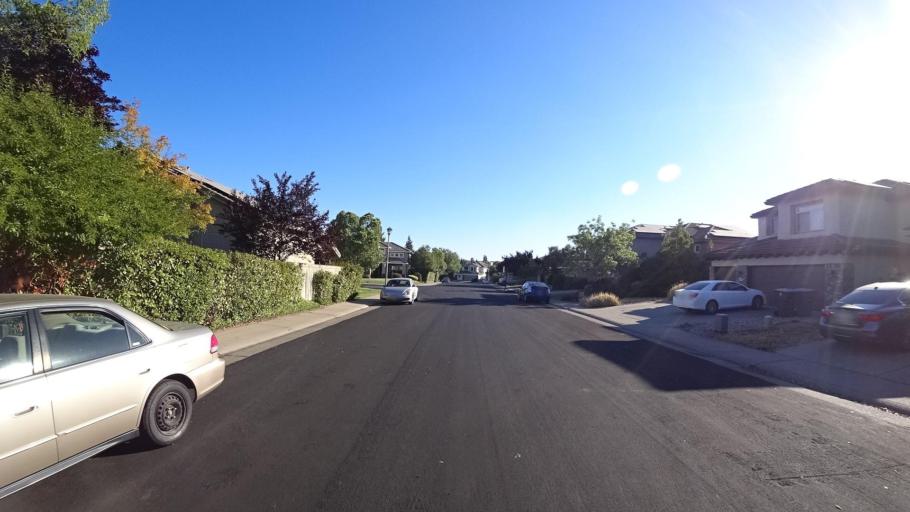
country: US
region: California
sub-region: Placer County
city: Rocklin
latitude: 38.8206
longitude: -121.2691
